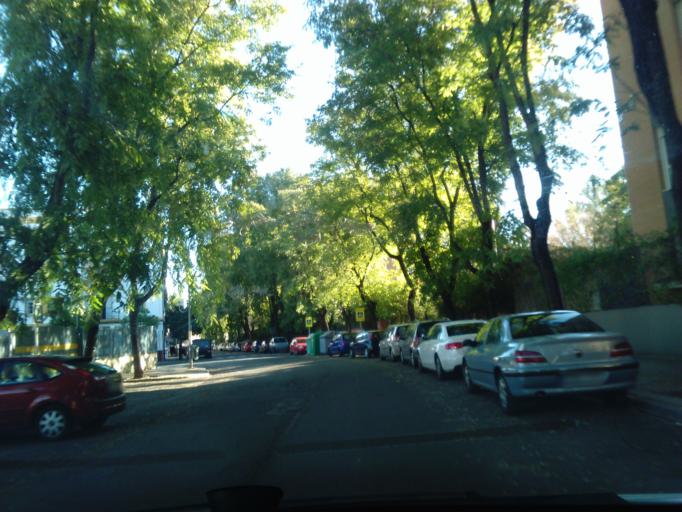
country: ES
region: Andalusia
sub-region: Provincia de Sevilla
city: Sevilla
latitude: 37.3553
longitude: -5.9786
